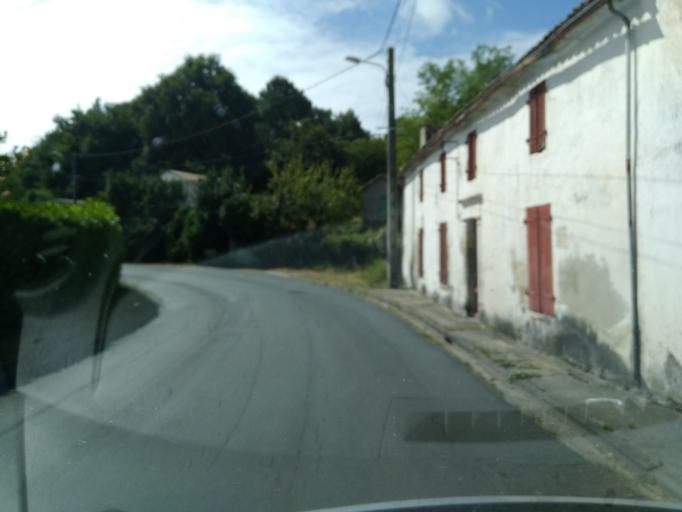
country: FR
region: Poitou-Charentes
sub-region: Departement de la Charente-Maritime
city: Saint-Palais-sur-Mer
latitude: 45.6701
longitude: -1.0849
